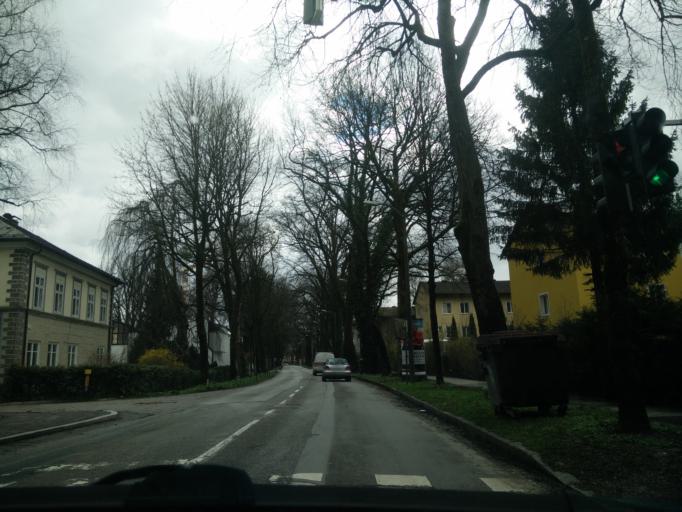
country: AT
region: Salzburg
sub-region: Salzburg Stadt
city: Salzburg
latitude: 47.7895
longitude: 13.0478
